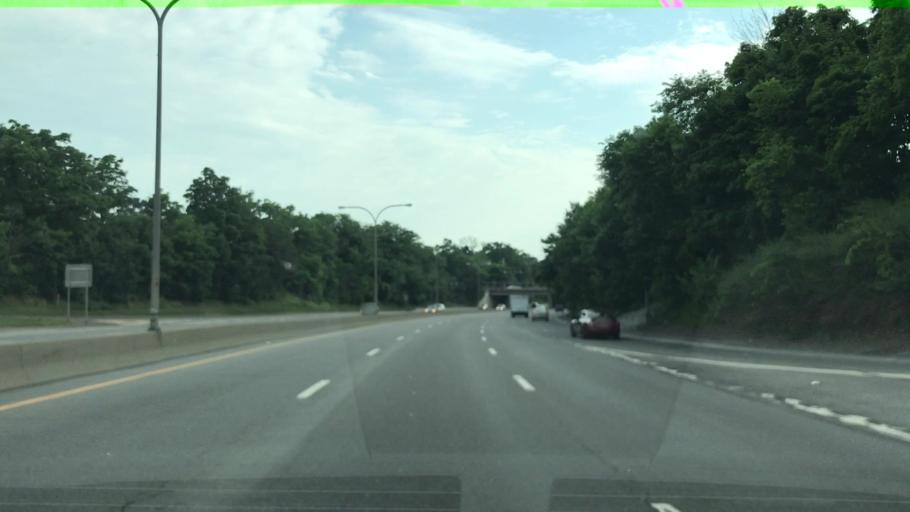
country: US
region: New York
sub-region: Erie County
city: Buffalo
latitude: 42.9023
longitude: -78.8468
